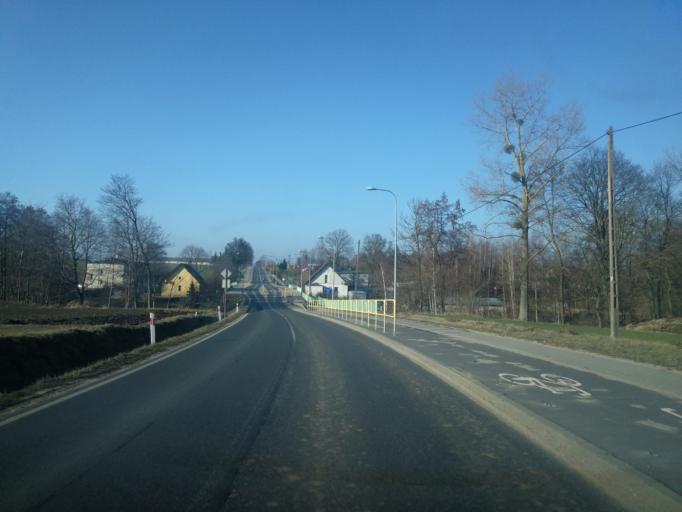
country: PL
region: Warmian-Masurian Voivodeship
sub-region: Powiat ilawski
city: Lubawa
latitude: 53.4553
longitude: 19.7790
